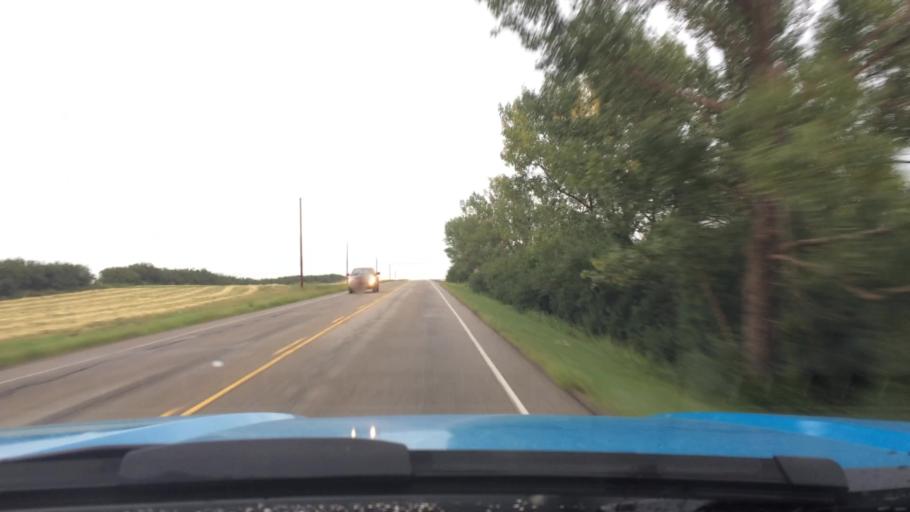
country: CA
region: Alberta
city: Airdrie
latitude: 51.2124
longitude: -114.0589
